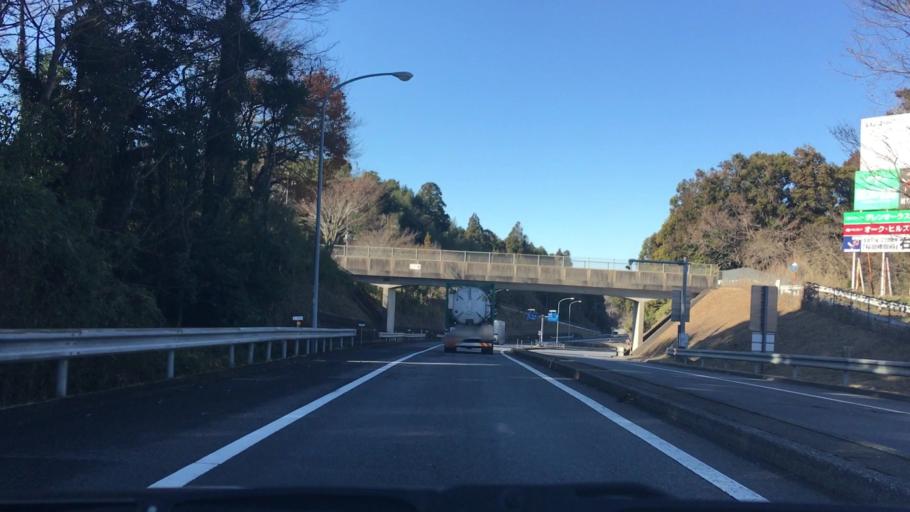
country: JP
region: Chiba
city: Sawara
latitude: 35.8408
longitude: 140.4463
